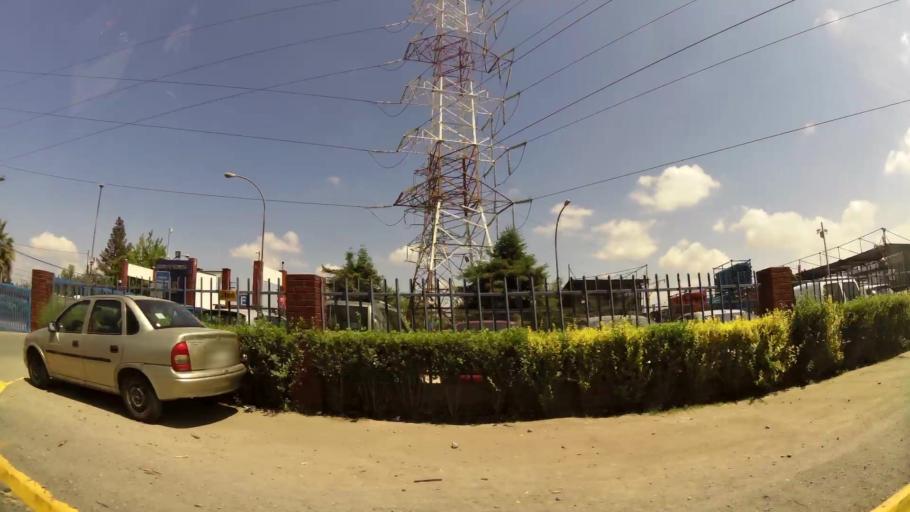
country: CL
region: Santiago Metropolitan
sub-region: Provincia de Maipo
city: San Bernardo
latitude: -33.5280
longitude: -70.7298
